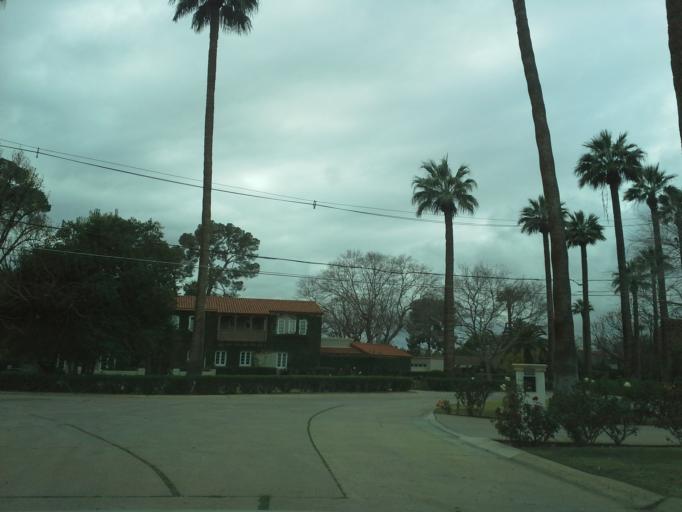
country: US
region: Arizona
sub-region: Maricopa County
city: Phoenix
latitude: 33.4812
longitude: -112.0574
